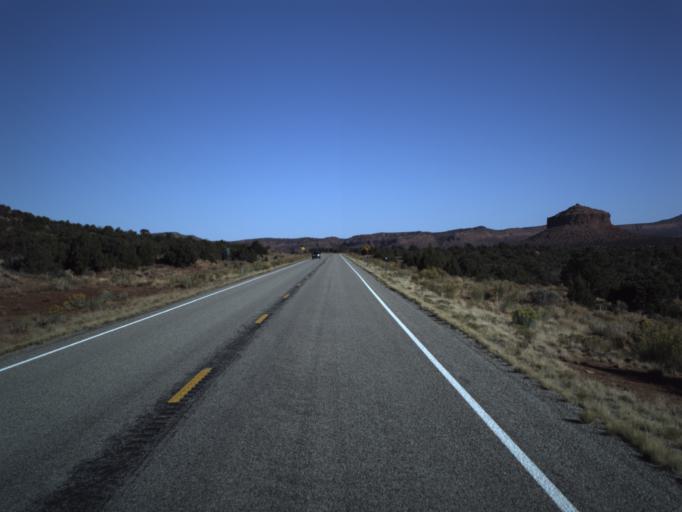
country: US
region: Utah
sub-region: San Juan County
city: Blanding
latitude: 37.6239
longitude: -110.0856
